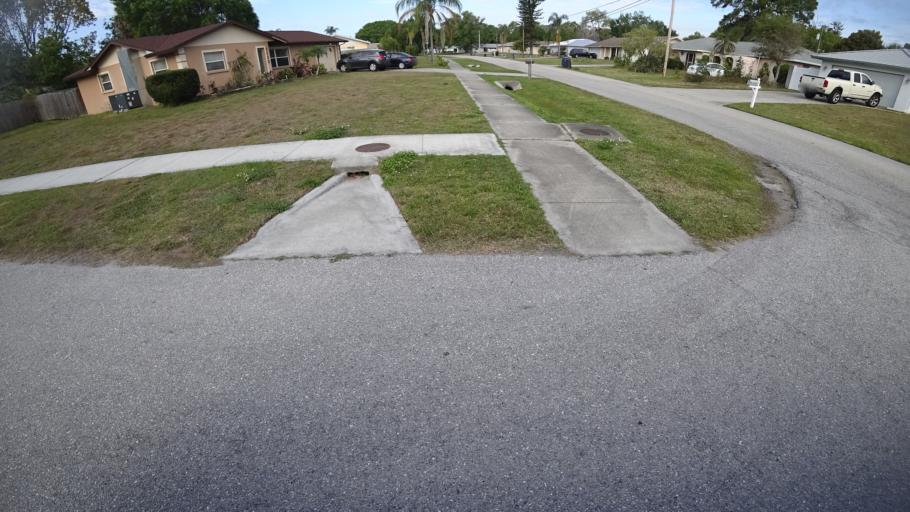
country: US
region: Florida
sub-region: Manatee County
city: Whitfield
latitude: 27.4223
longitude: -82.5513
